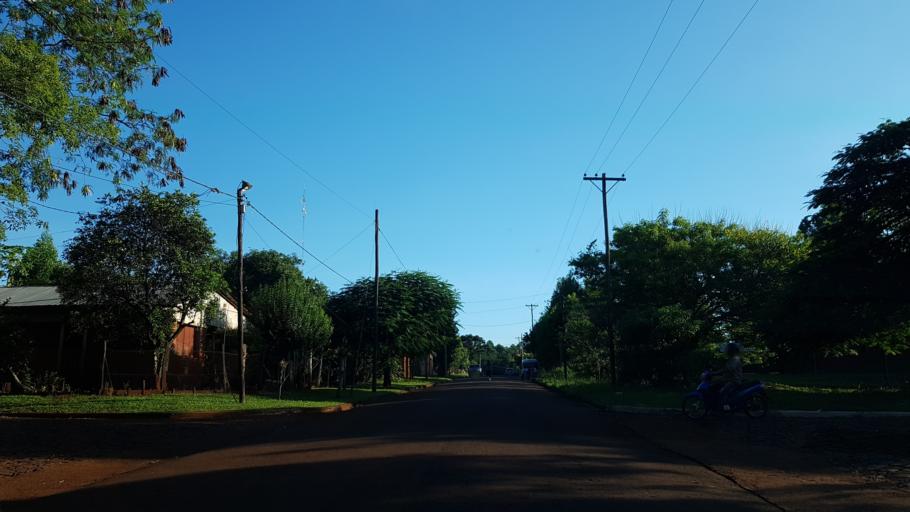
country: AR
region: Misiones
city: Puerto Libertad
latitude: -25.9221
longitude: -54.5873
